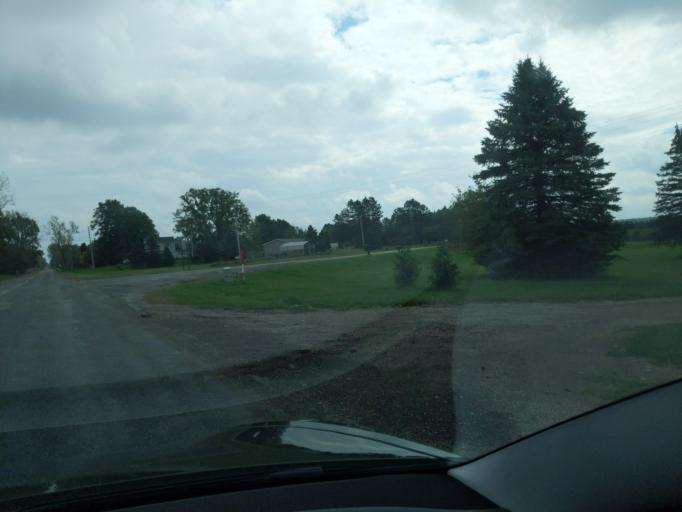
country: US
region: Michigan
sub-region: Eaton County
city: Eaton Rapids
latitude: 42.4838
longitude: -84.6405
